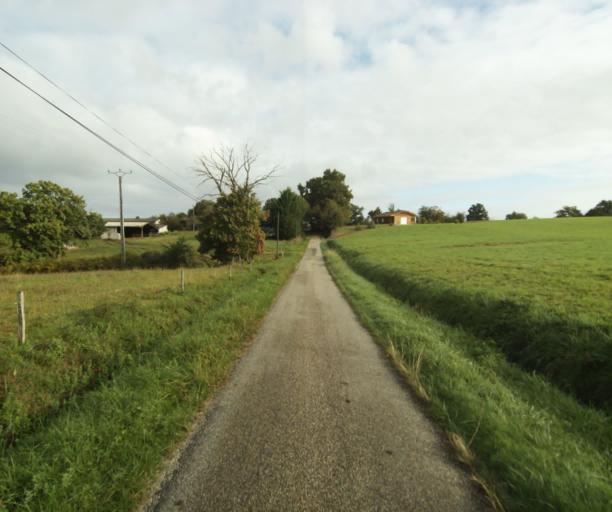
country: FR
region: Midi-Pyrenees
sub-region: Departement du Gers
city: Nogaro
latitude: 43.8163
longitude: -0.0617
